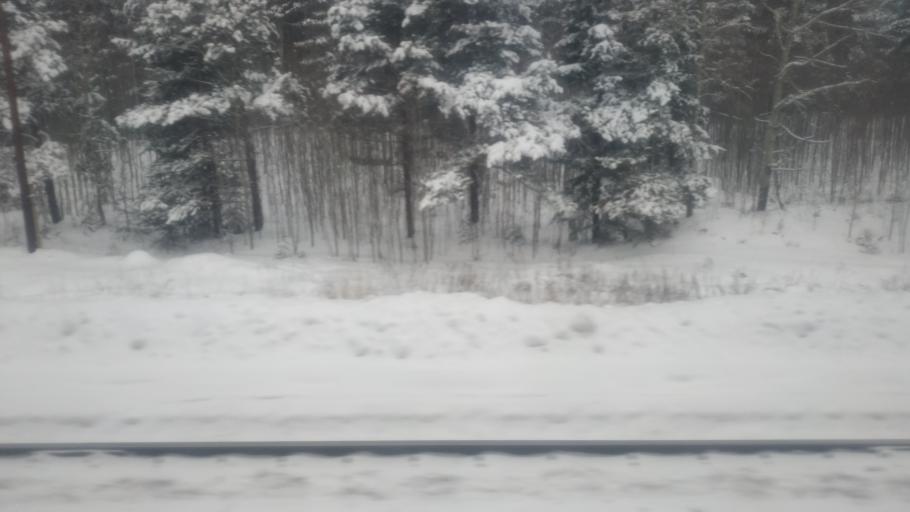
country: RU
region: Udmurtiya
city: Kama
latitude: 56.2913
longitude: 54.1210
